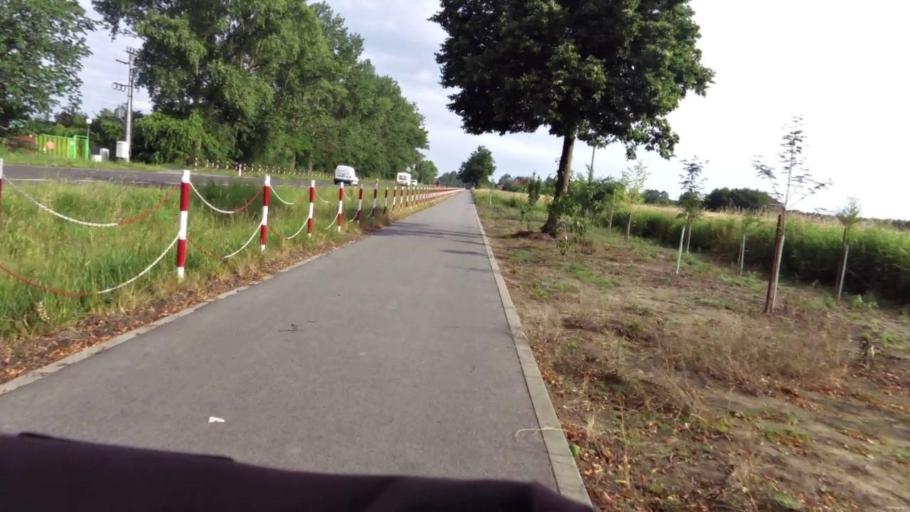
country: PL
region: West Pomeranian Voivodeship
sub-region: Powiat kamienski
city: Dziwnow
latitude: 54.0226
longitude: 14.8096
